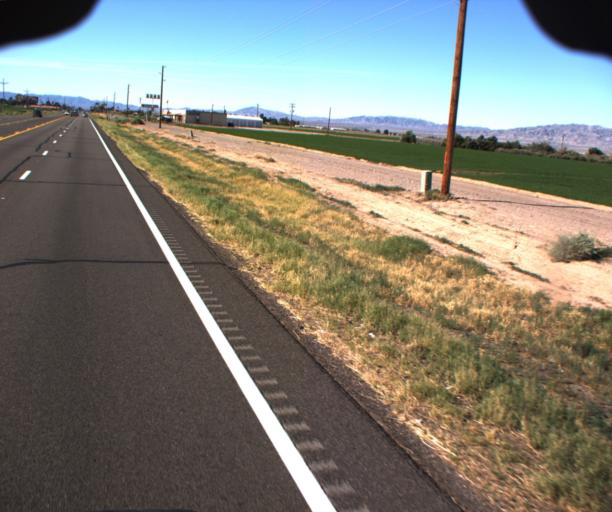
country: US
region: Arizona
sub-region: Mohave County
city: Willow Valley
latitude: 34.9212
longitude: -114.5979
